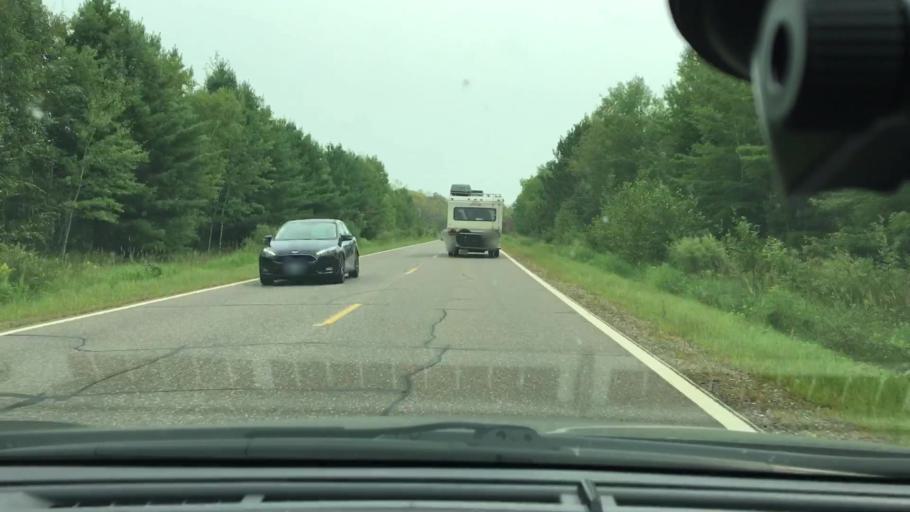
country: US
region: Minnesota
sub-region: Aitkin County
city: Aitkin
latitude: 46.4026
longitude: -93.7569
